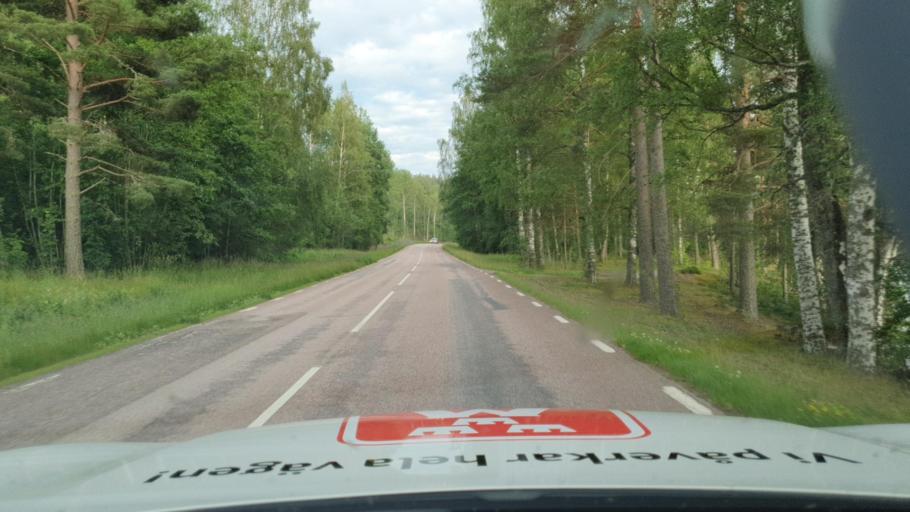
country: SE
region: Vaermland
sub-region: Karlstads Kommun
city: Molkom
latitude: 59.5876
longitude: 13.7392
